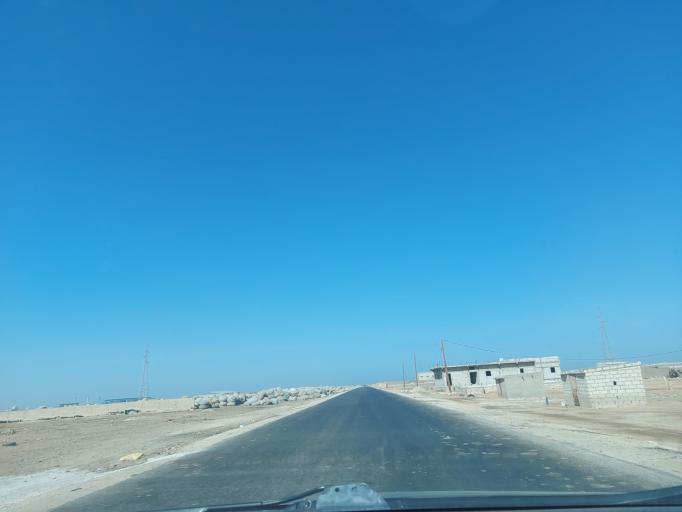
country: MR
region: Nouakchott
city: Nouakchott
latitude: 18.0601
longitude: -16.0088
